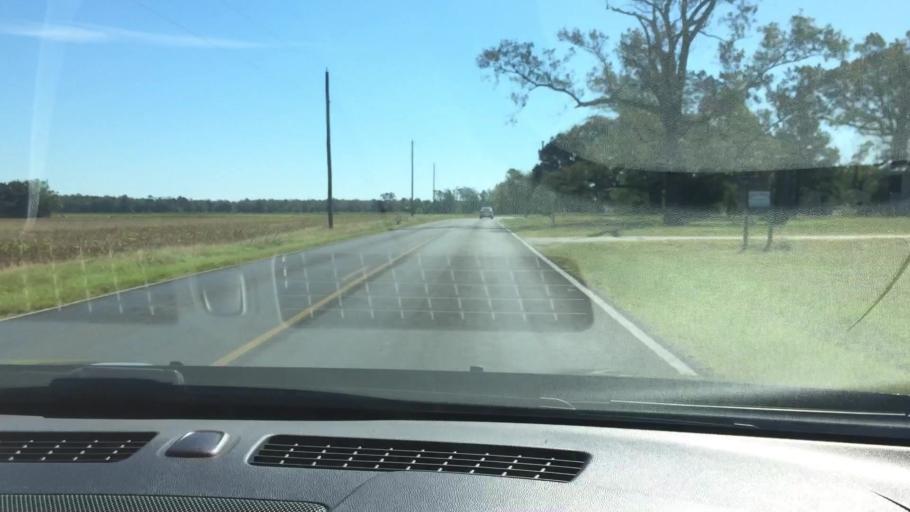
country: US
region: North Carolina
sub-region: Pitt County
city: Grifton
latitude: 35.3707
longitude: -77.3549
